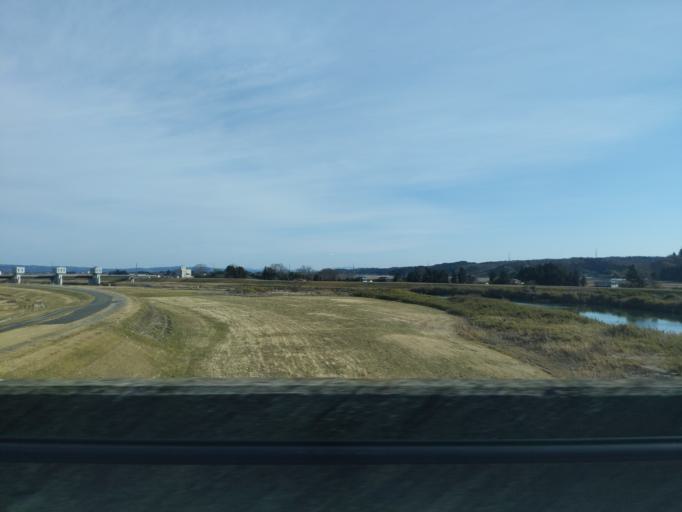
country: JP
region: Miyagi
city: Furukawa
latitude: 38.5256
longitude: 140.9604
